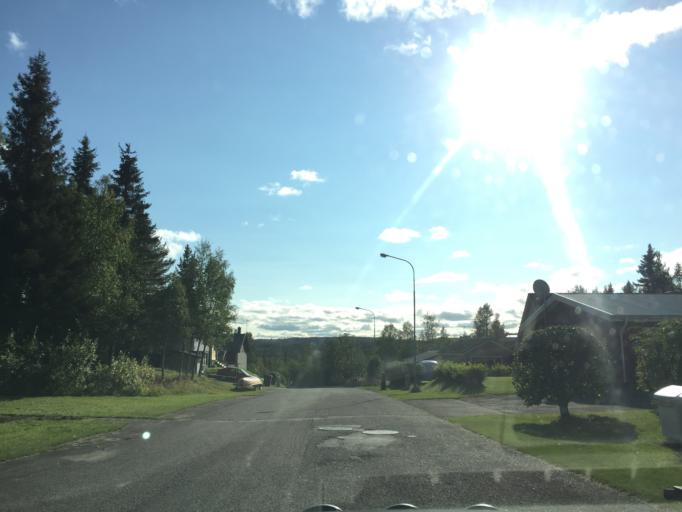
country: SE
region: Norrbotten
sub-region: Gallivare Kommun
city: Malmberget
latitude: 67.6527
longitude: 21.0457
